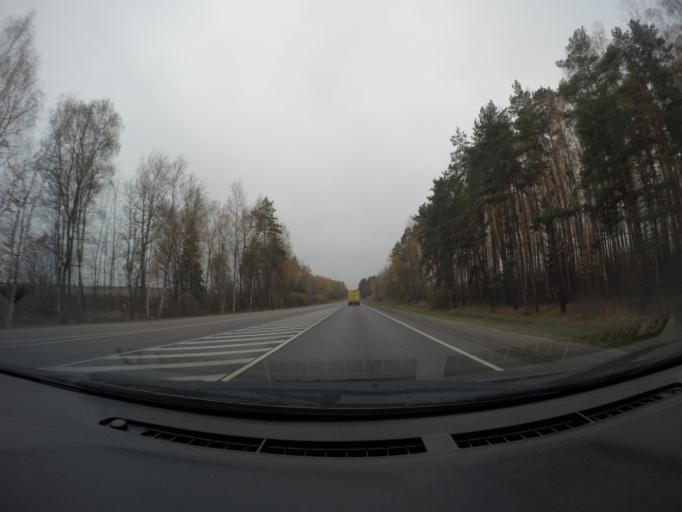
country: RU
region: Moskovskaya
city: Malyshevo
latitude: 55.5257
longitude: 38.3961
